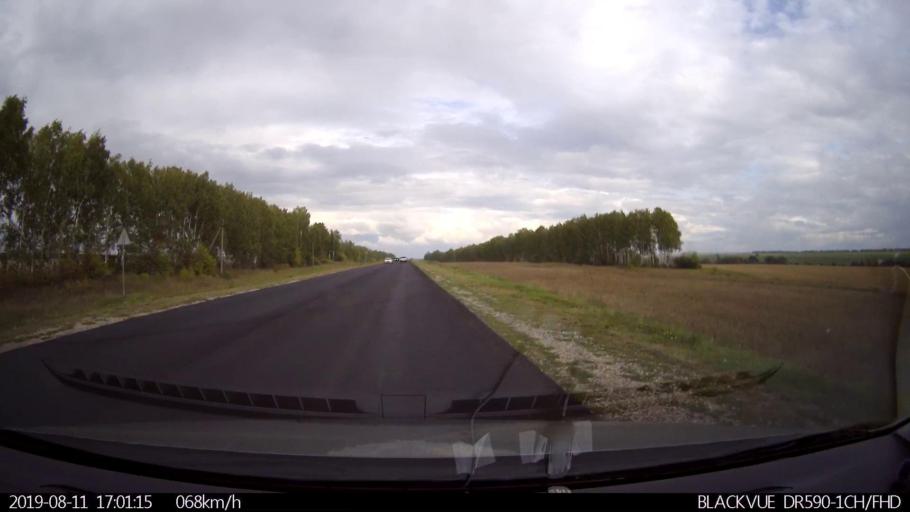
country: RU
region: Ulyanovsk
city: Mayna
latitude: 54.3085
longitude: 47.6940
